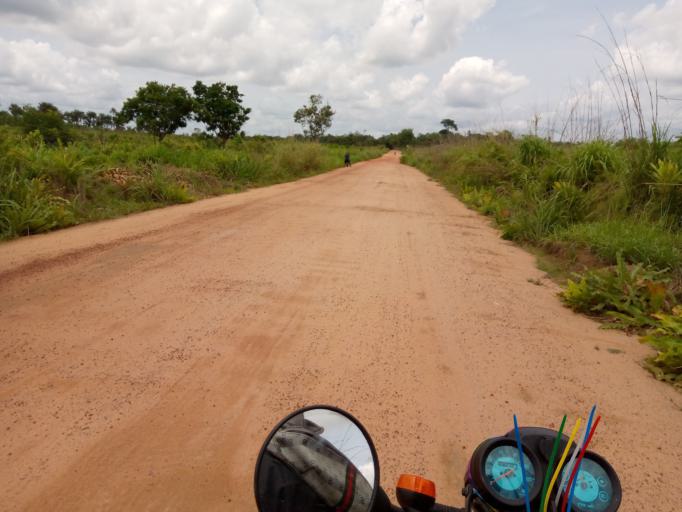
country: SL
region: Western Area
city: Waterloo
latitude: 8.3413
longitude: -12.9461
